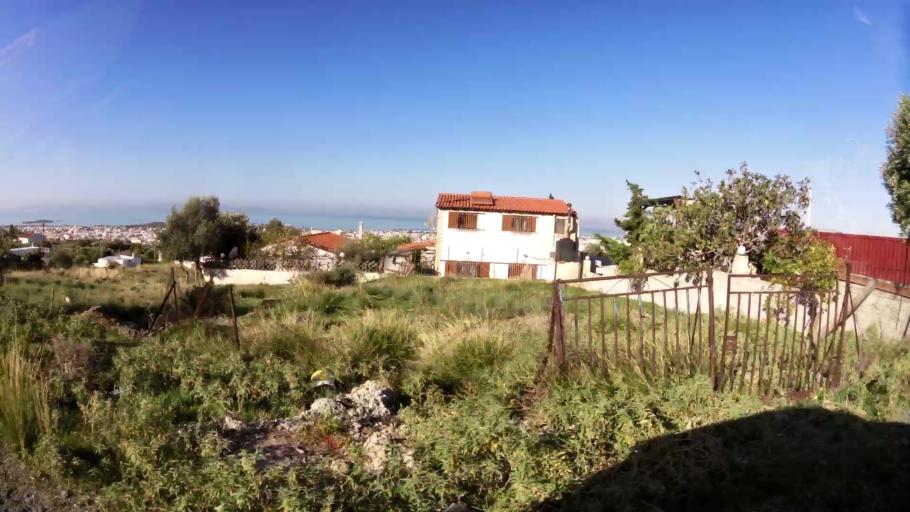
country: GR
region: Attica
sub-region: Nomarchia Athinas
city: Glyfada
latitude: 37.8719
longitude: 23.7754
